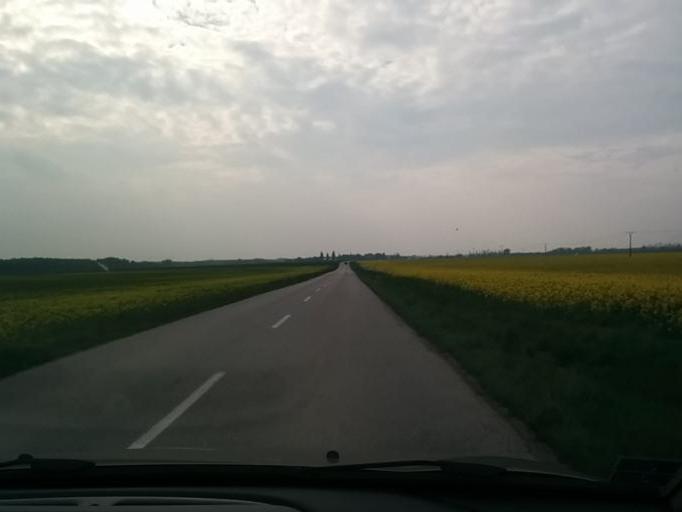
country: SK
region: Trnavsky
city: Sladkovicovo
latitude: 48.2096
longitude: 17.6173
